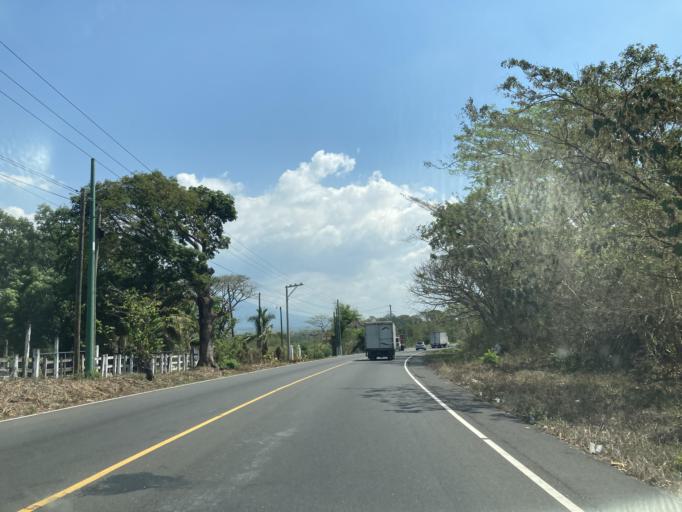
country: GT
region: Santa Rosa
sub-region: Municipio de Taxisco
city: Taxisco
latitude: 14.0972
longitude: -90.5971
